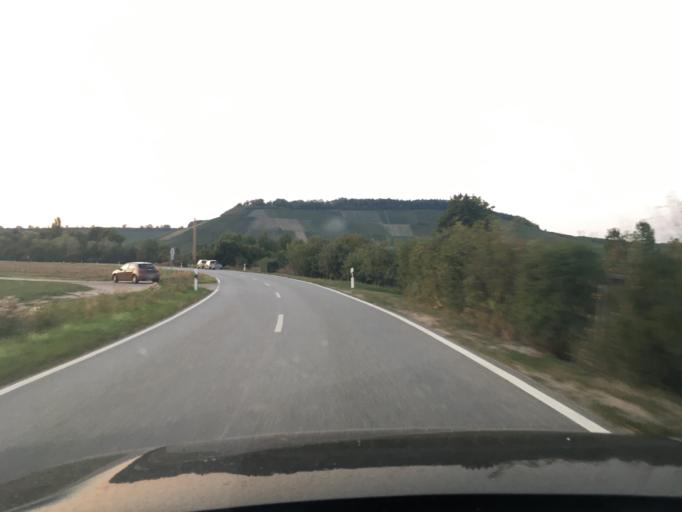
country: DE
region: Baden-Wuerttemberg
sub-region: Regierungsbezirk Stuttgart
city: Brackenheim
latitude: 49.0917
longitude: 9.0770
